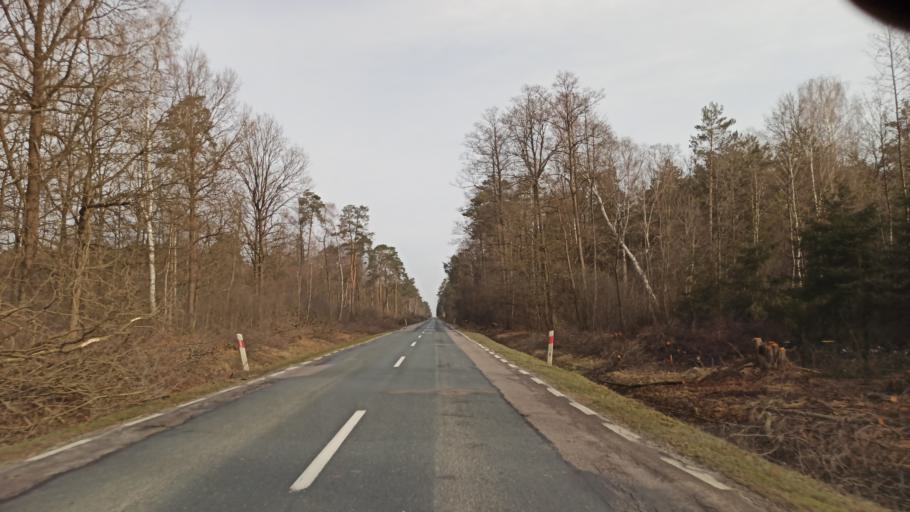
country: PL
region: Lublin Voivodeship
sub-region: Powiat bilgorajski
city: Tarnogrod
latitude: 50.3078
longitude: 22.7238
